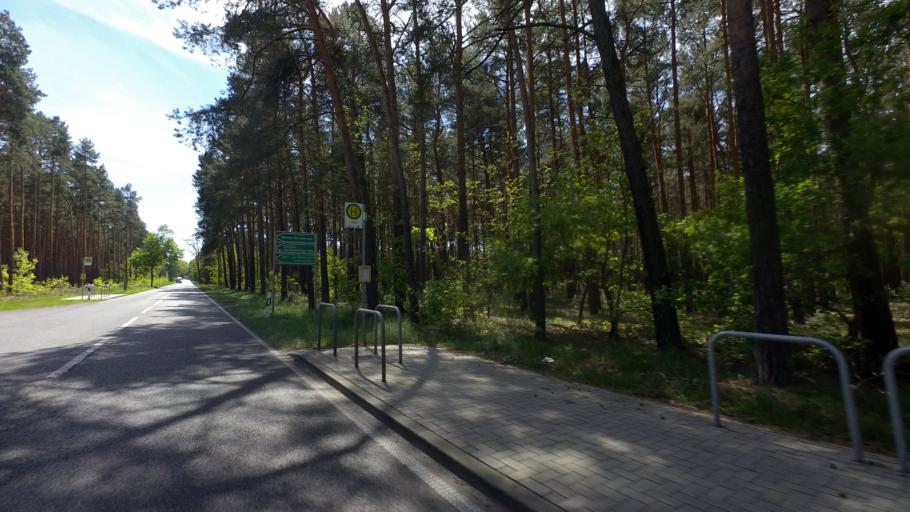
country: DE
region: Brandenburg
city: Luckenwalde
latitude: 52.1540
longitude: 13.1061
